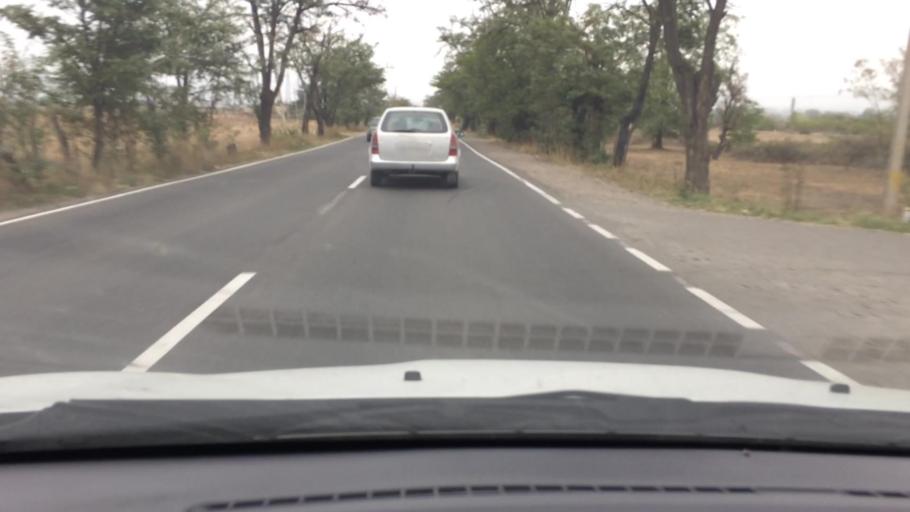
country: GE
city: Naghvarevi
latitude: 41.3866
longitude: 44.8292
